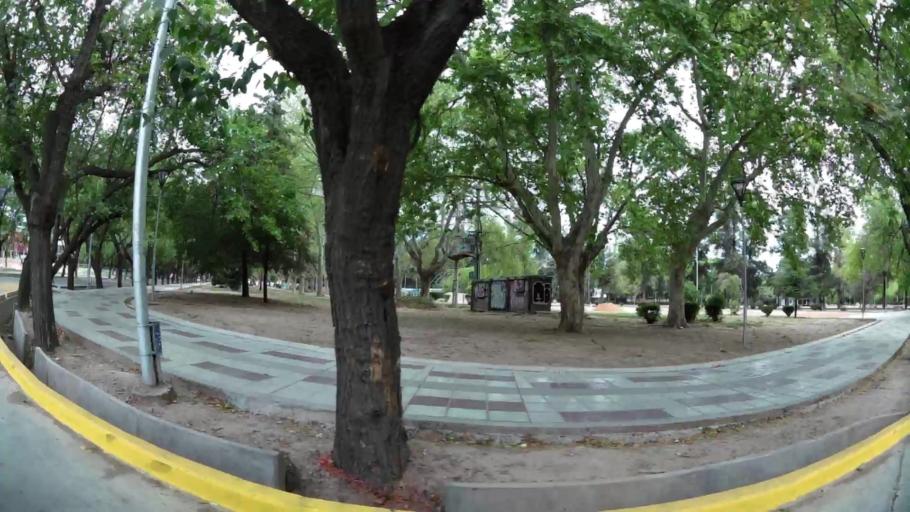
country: AR
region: Mendoza
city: Mendoza
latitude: -32.8979
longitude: -68.8482
